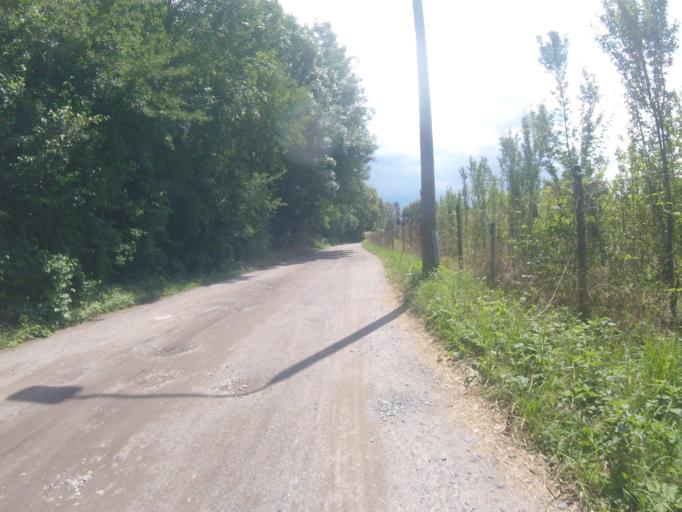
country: DE
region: Brandenburg
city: Bestensee
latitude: 52.2661
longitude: 13.6430
